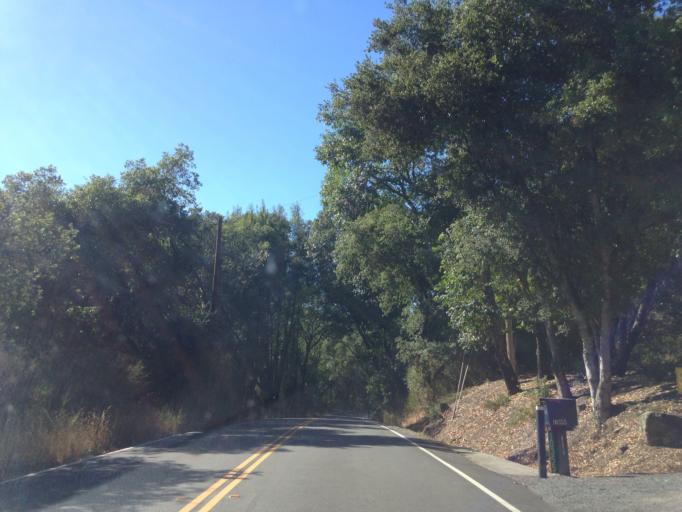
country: US
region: California
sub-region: Sonoma County
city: Forestville
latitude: 38.5021
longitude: -122.8978
